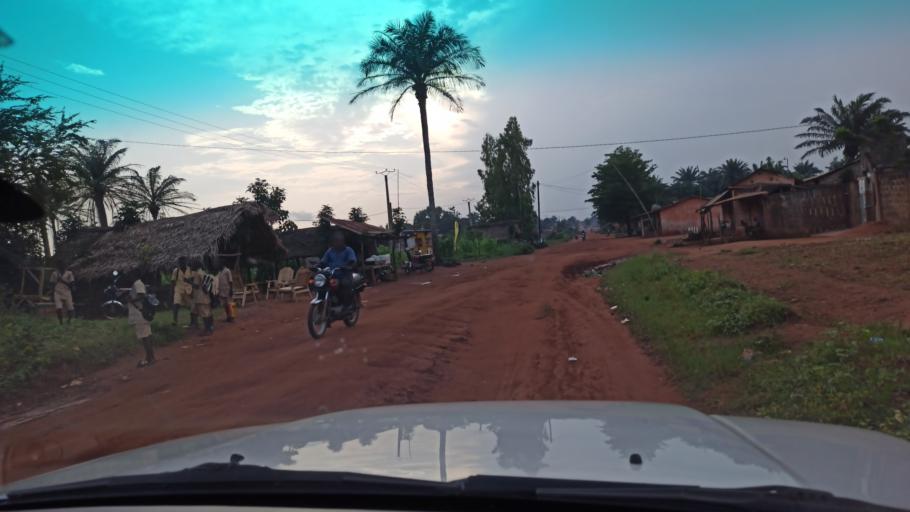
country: BJ
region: Queme
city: Porto-Novo
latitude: 6.5351
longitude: 2.6520
